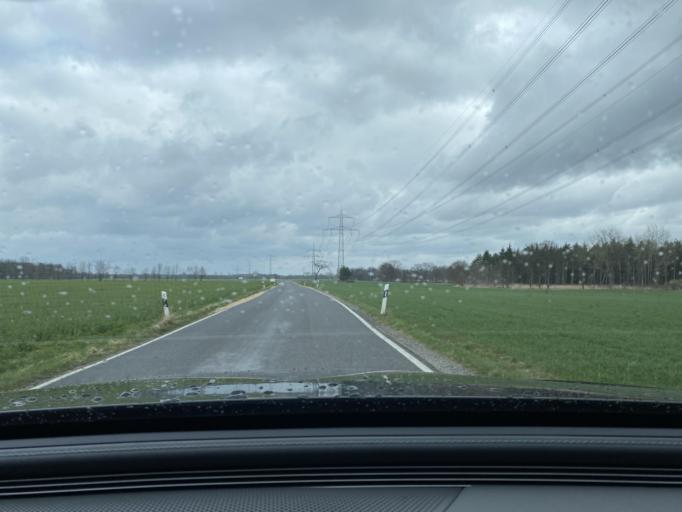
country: DE
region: Saxony
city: Grossdubrau
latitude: 51.2844
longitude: 14.4402
